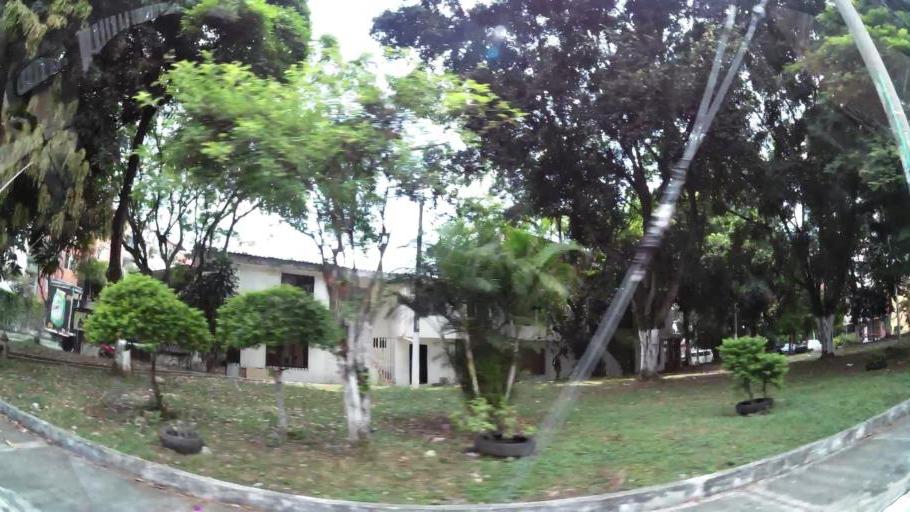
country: CO
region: Valle del Cauca
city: Cali
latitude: 3.4748
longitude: -76.5032
